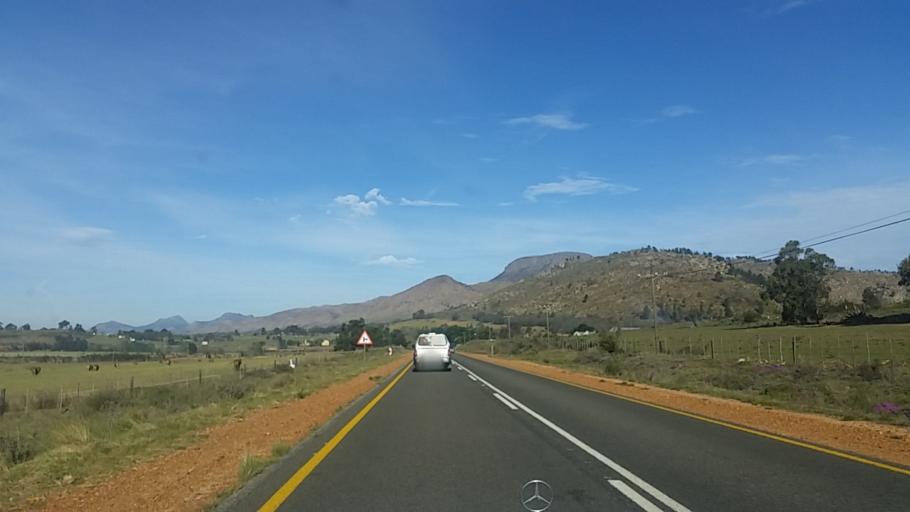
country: ZA
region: Western Cape
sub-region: Eden District Municipality
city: George
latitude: -33.8324
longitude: 22.4363
